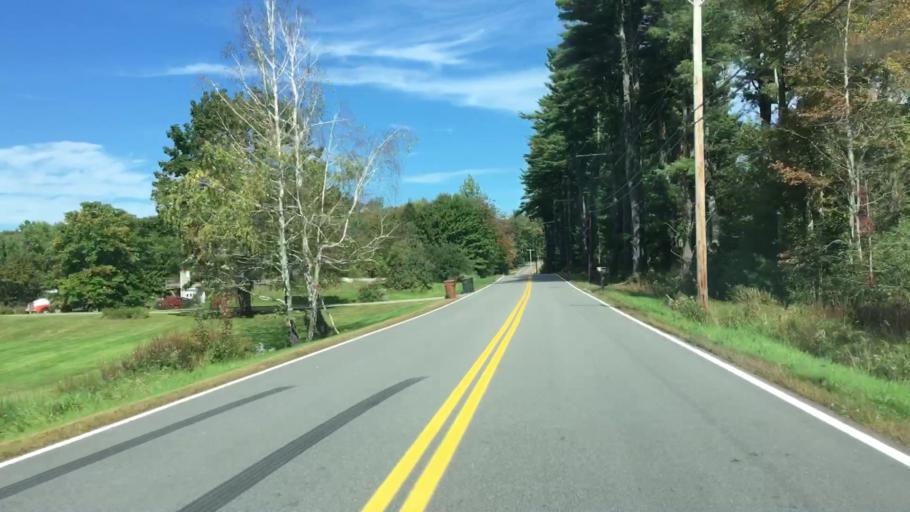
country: US
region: Maine
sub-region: York County
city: Saco
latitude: 43.5655
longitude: -70.4851
